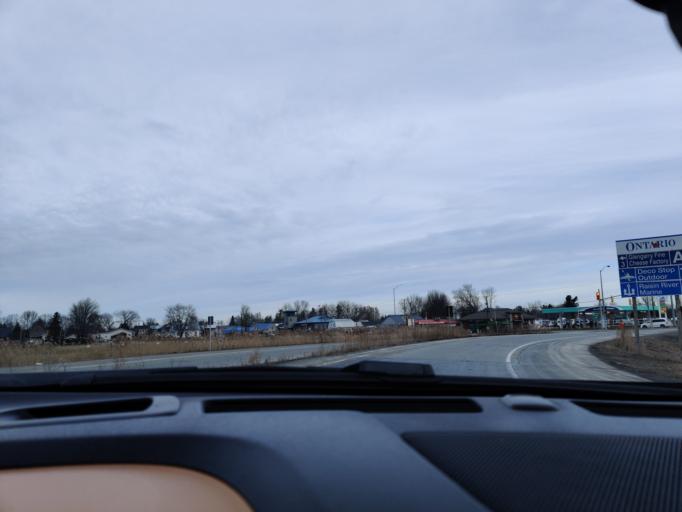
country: CA
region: Ontario
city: Cornwall
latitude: 45.1375
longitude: -74.4991
